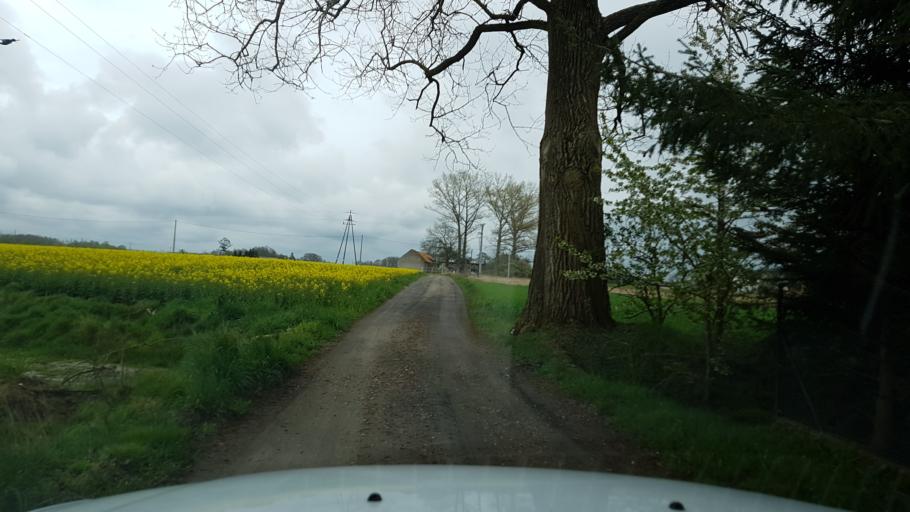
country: PL
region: West Pomeranian Voivodeship
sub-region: Powiat kolobrzeski
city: Ryman
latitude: 54.0340
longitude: 15.4764
